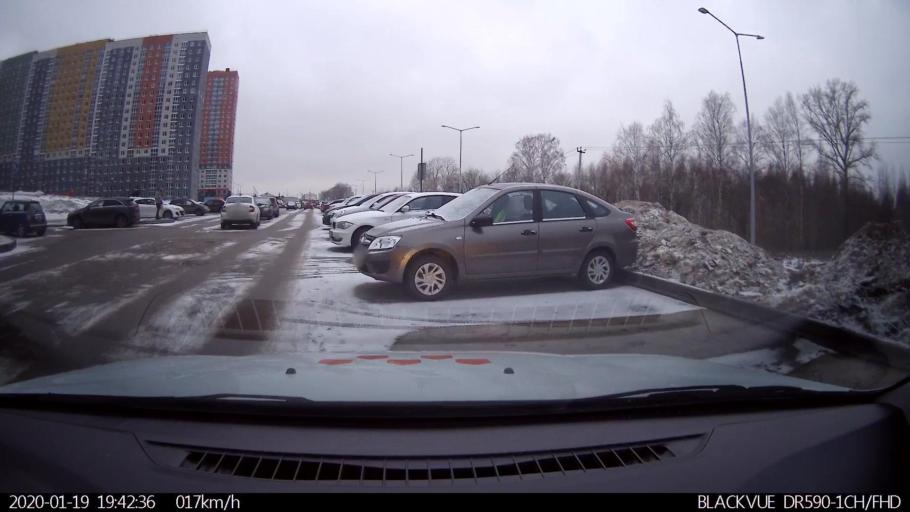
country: RU
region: Nizjnij Novgorod
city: Afonino
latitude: 56.2500
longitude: 44.0466
